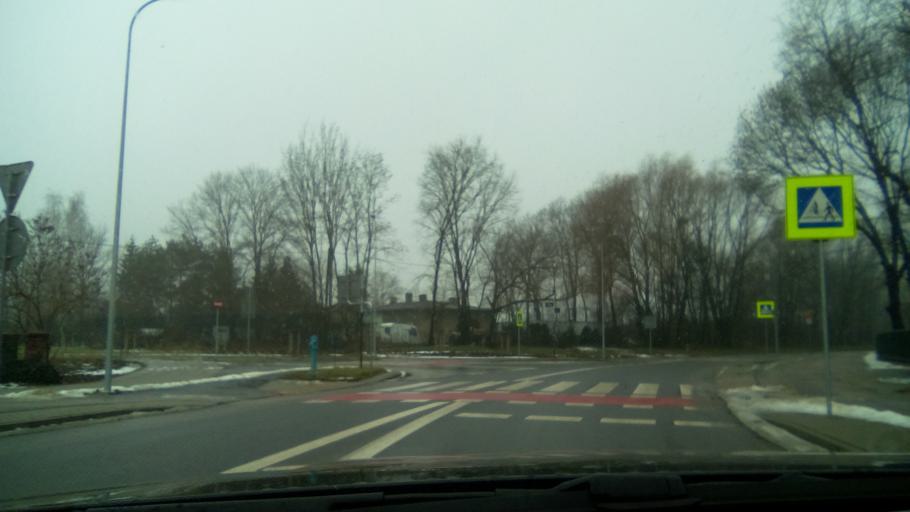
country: PL
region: Greater Poland Voivodeship
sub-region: Powiat poznanski
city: Swarzedz
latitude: 52.3909
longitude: 17.0144
